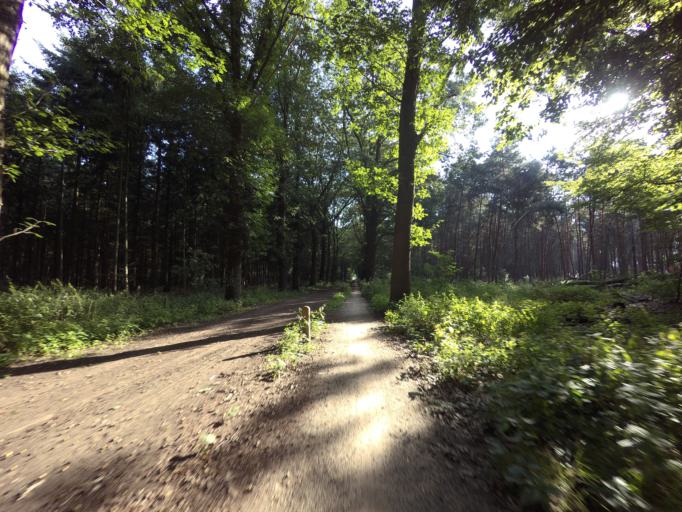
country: NL
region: Gelderland
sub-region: Oude IJsselstreek
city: Wisch
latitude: 51.9189
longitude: 6.4245
